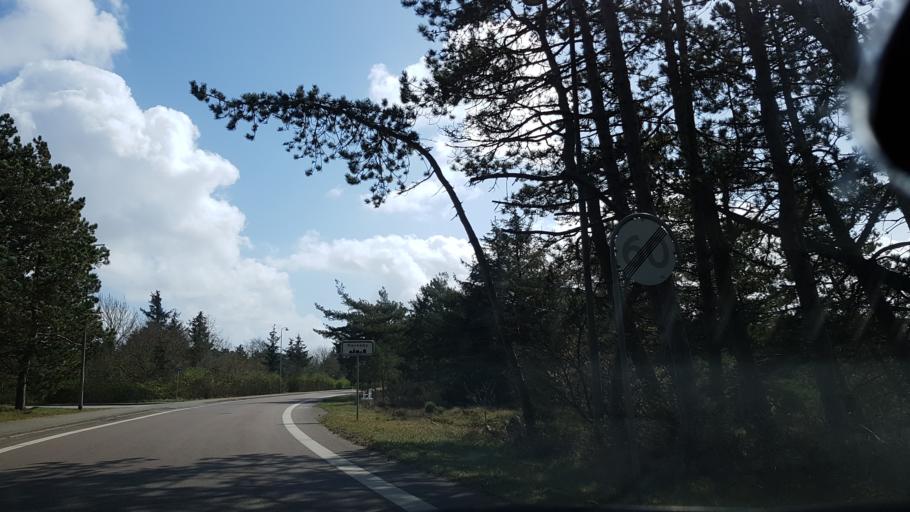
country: DE
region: Schleswig-Holstein
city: List
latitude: 55.0925
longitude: 8.5508
